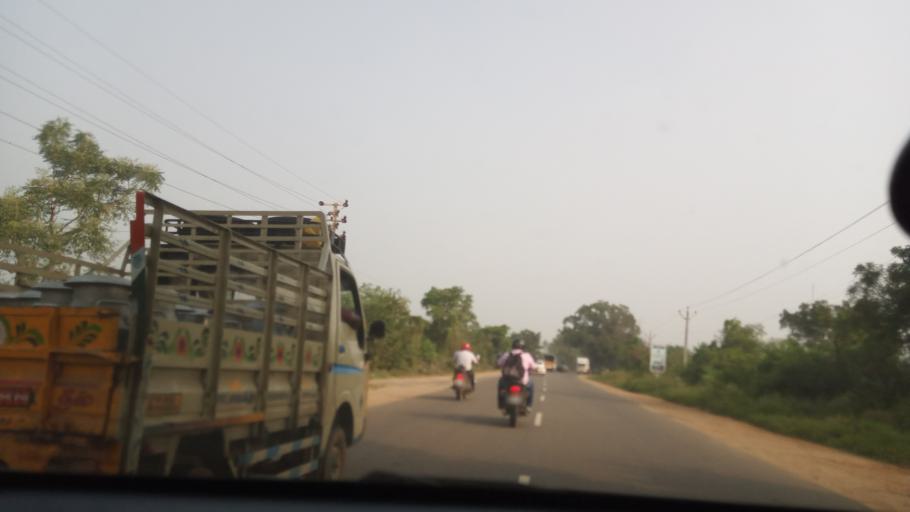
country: IN
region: Tamil Nadu
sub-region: Coimbatore
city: Annur
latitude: 11.1634
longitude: 77.0520
